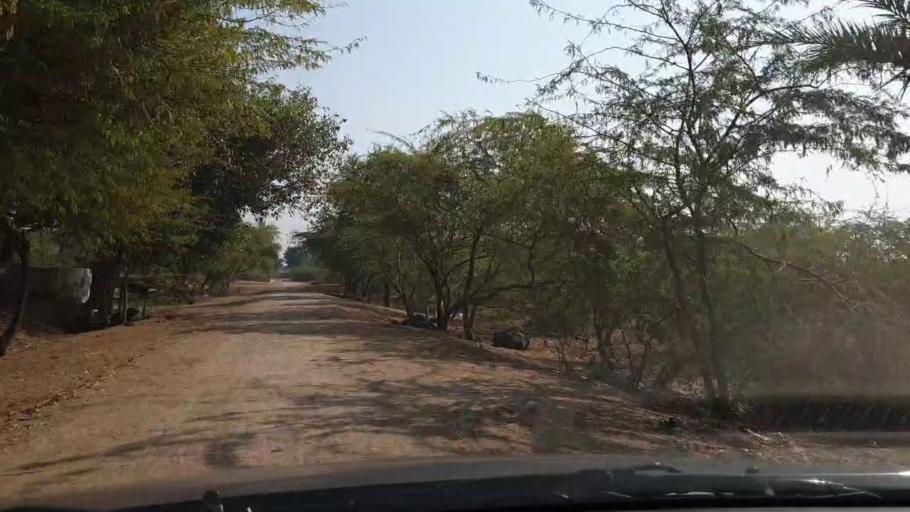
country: PK
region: Sindh
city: Jhol
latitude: 25.9345
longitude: 68.9956
